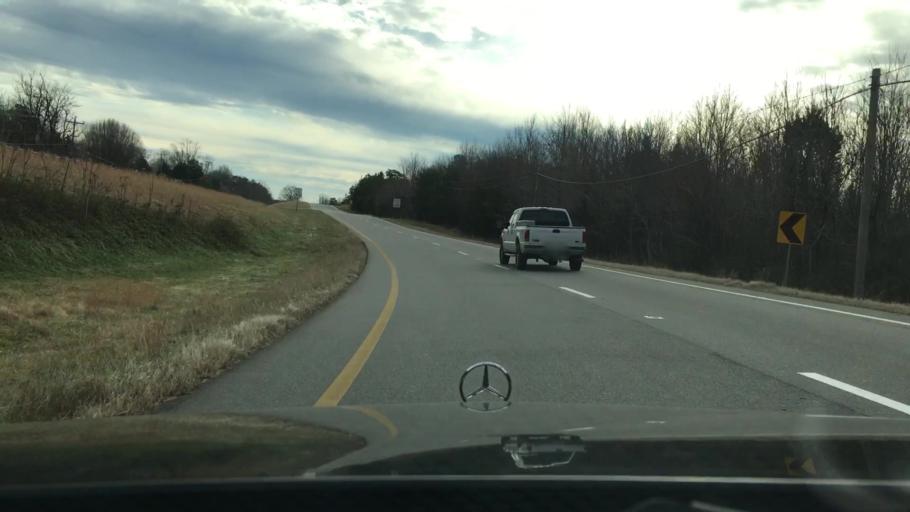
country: US
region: Virginia
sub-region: Pittsylvania County
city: Chatham
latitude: 36.8832
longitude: -79.4082
